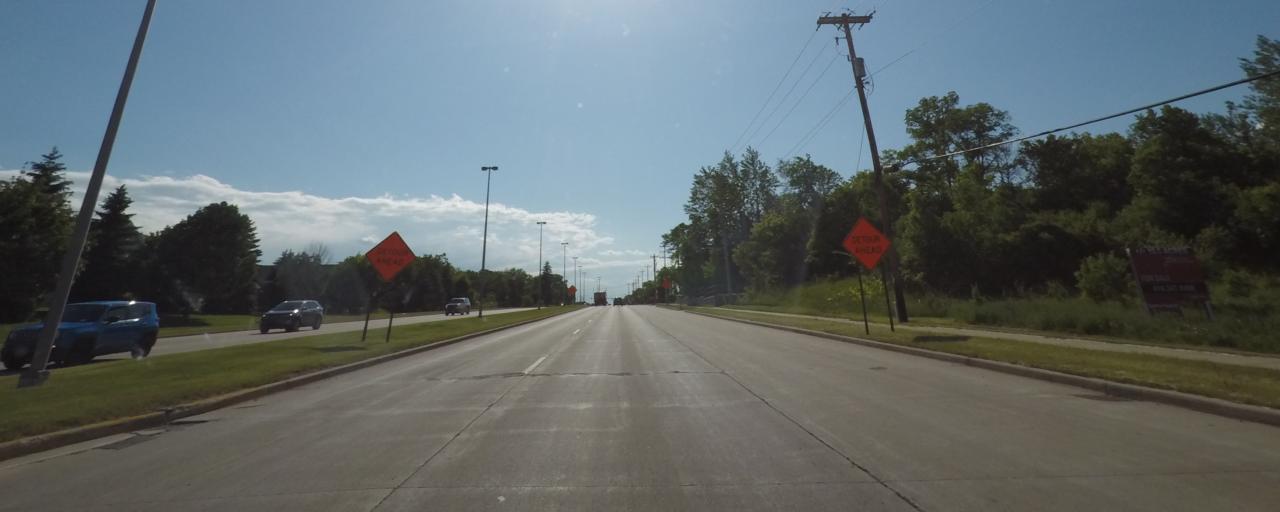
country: US
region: Wisconsin
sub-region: Milwaukee County
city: Greendale
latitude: 42.9161
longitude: -88.0022
